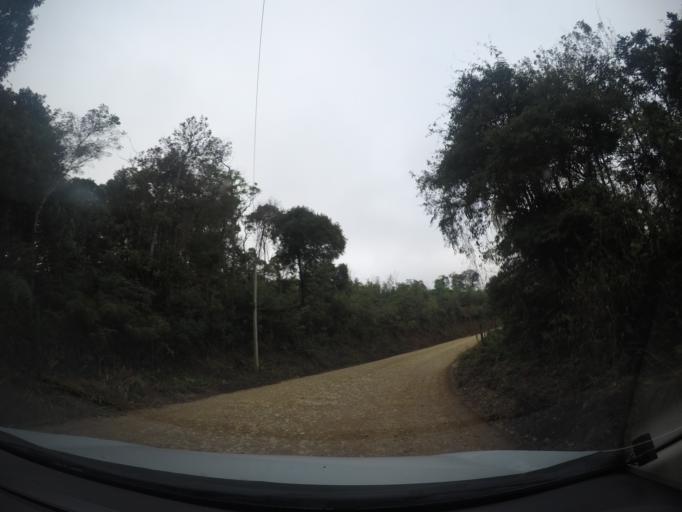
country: BR
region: Parana
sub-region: Colombo
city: Colombo
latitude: -25.3124
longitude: -49.2455
